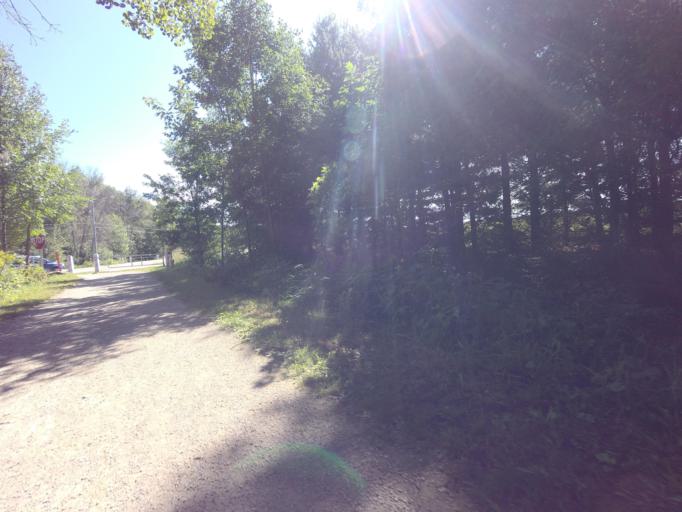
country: CA
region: Ontario
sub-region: Wellington County
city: Guelph
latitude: 43.6989
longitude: -80.3988
